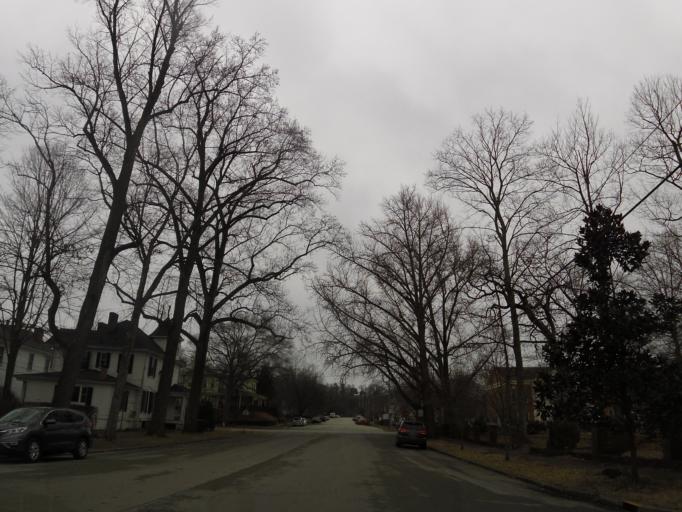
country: US
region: Kentucky
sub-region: Franklin County
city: Frankfort
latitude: 38.1922
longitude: -84.8758
